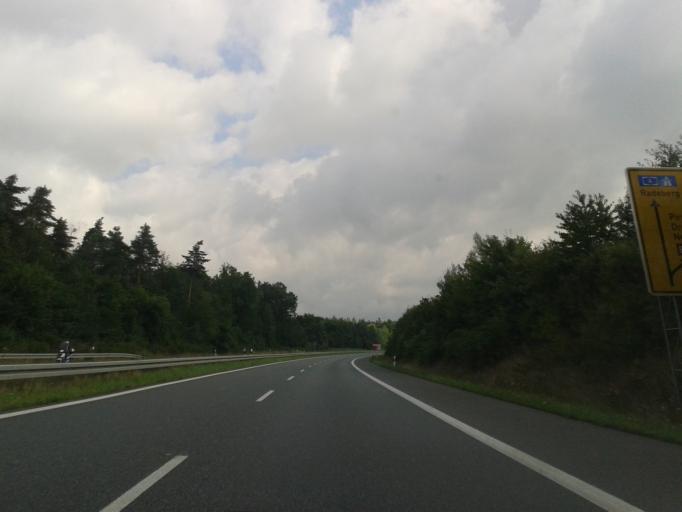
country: DE
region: Saxony
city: Pirna
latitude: 50.9810
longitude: 13.9179
